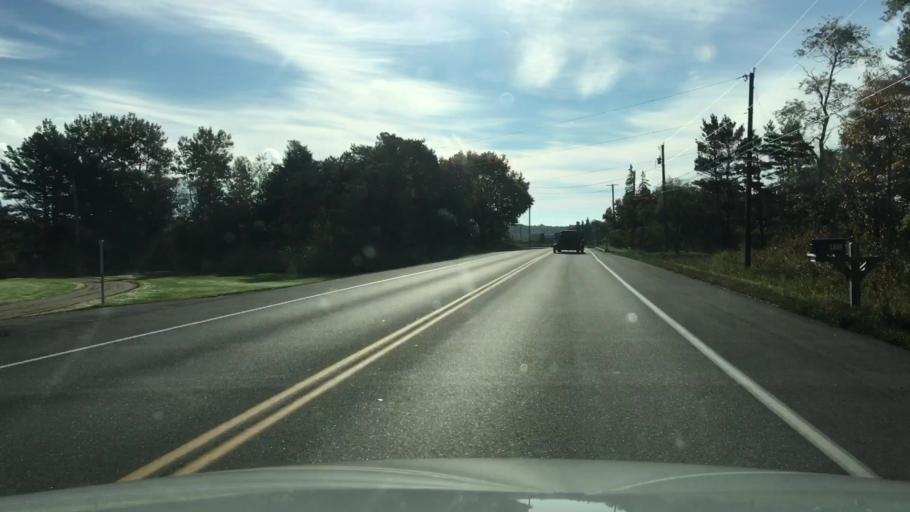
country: US
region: Maine
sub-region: Knox County
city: Warren
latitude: 44.0856
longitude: -69.2302
